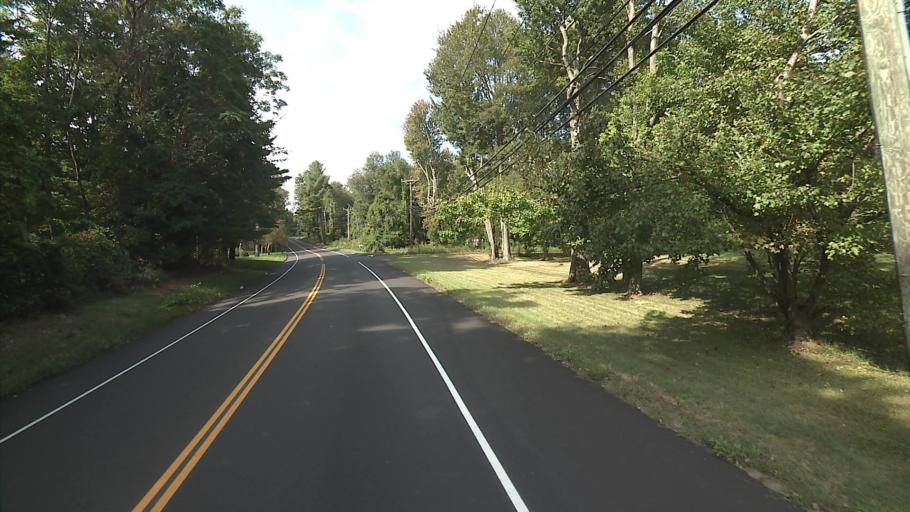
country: US
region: Connecticut
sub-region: Fairfield County
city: Newtown
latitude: 41.3912
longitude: -73.2161
